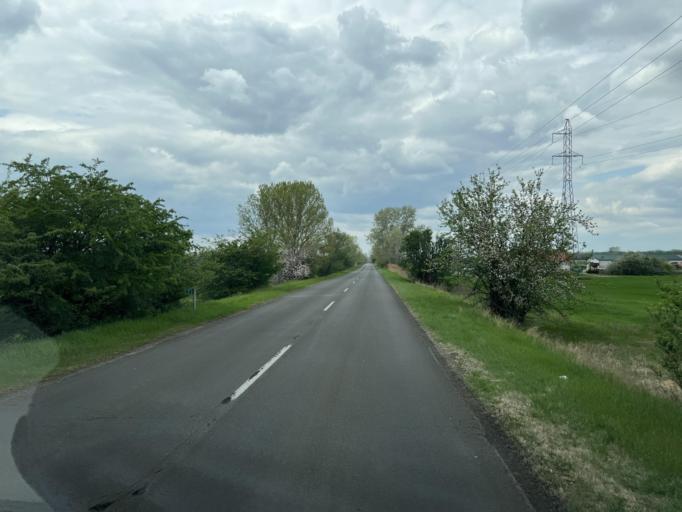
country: HU
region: Pest
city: Ujhartyan
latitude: 47.1991
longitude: 19.4075
